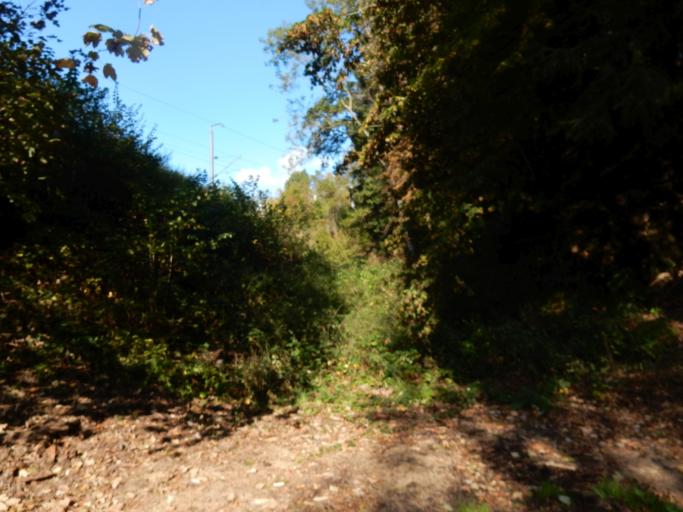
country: LU
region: Diekirch
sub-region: Canton de Clervaux
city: Clervaux
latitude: 50.0478
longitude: 6.0186
